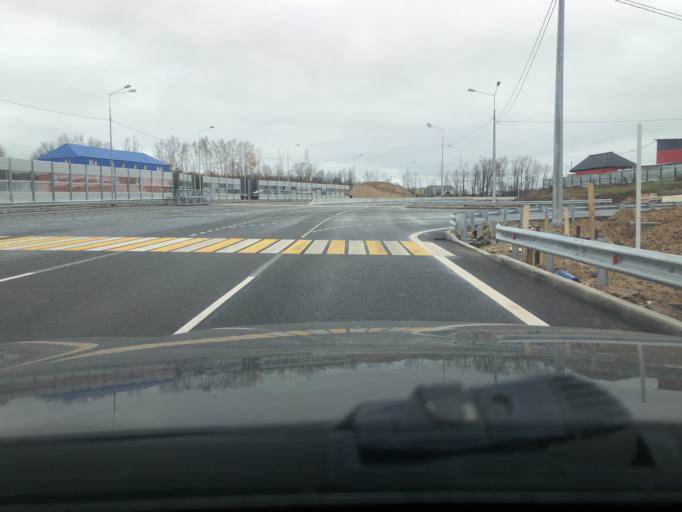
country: RU
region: Moskovskaya
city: Sergiyev Posad
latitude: 56.3404
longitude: 38.1218
